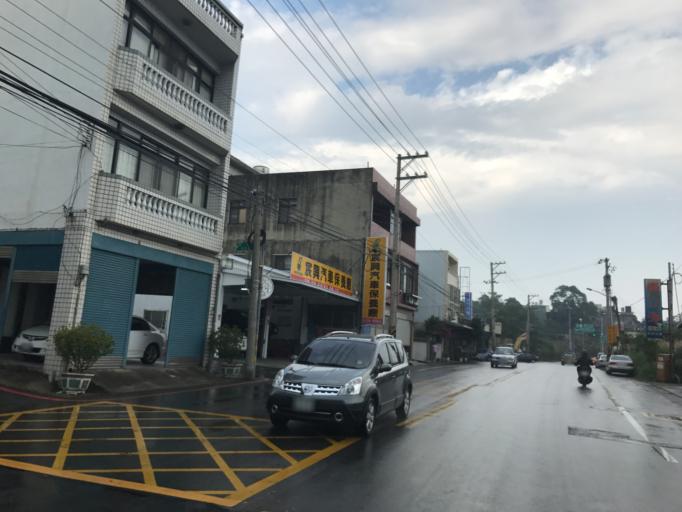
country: TW
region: Taiwan
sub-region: Hsinchu
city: Hsinchu
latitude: 24.7775
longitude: 120.9673
